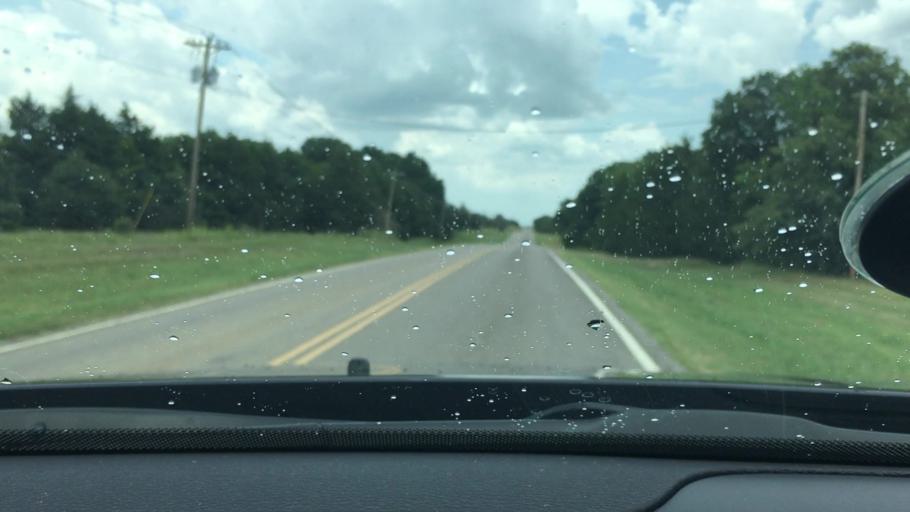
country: US
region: Oklahoma
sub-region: Love County
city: Marietta
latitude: 33.9466
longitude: -97.0354
